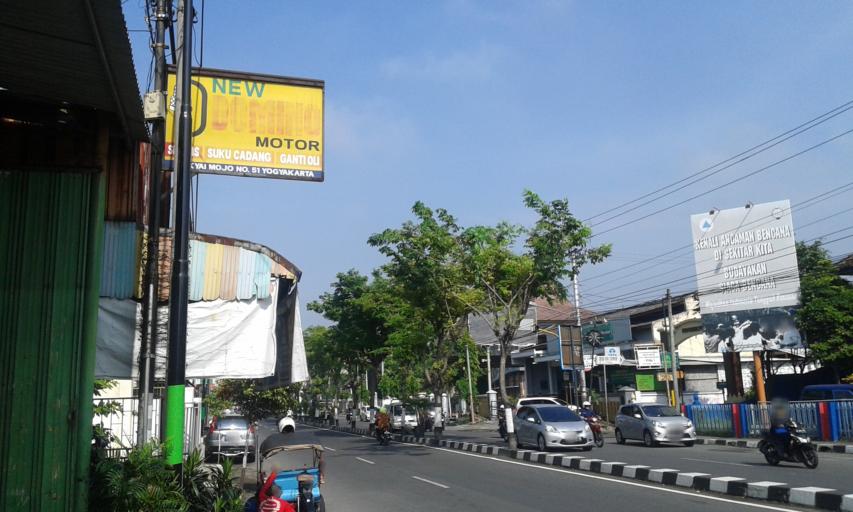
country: ID
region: Daerah Istimewa Yogyakarta
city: Yogyakarta
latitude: -7.7823
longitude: 110.3552
